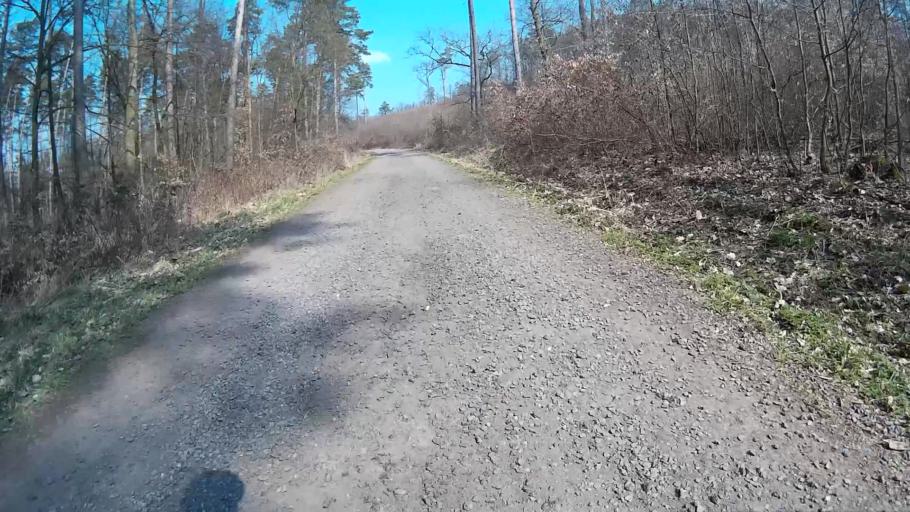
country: CZ
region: South Moravian
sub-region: Mesto Brno
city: Mokra Hora
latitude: 49.2563
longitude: 16.6083
